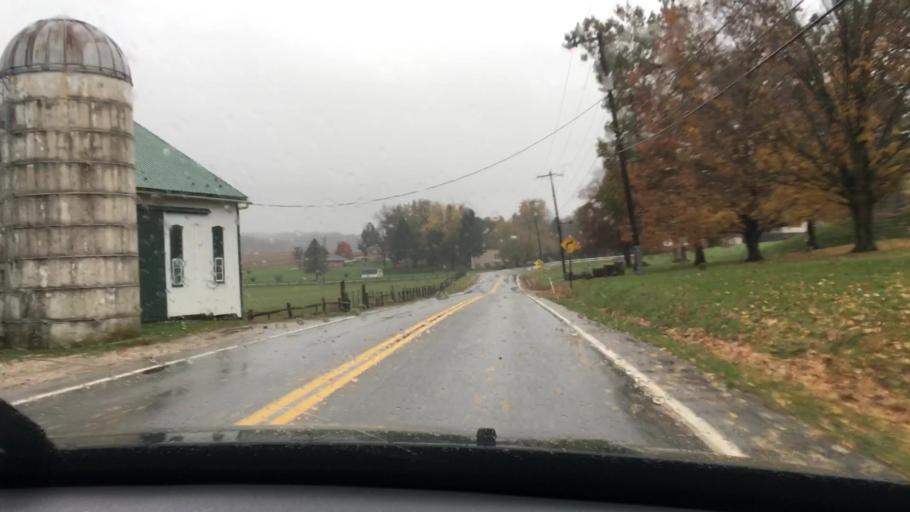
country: US
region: Pennsylvania
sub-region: York County
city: Glen Rock
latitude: 39.7693
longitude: -76.7319
